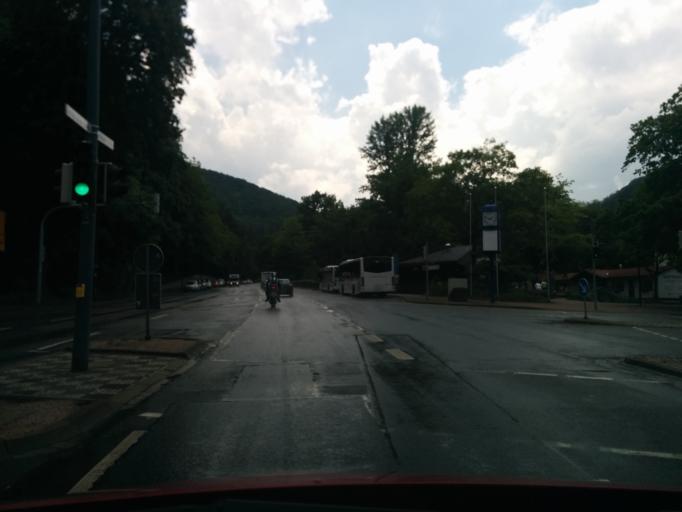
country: DE
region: Lower Saxony
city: Bad Harzburg
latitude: 51.8743
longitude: 10.5619
